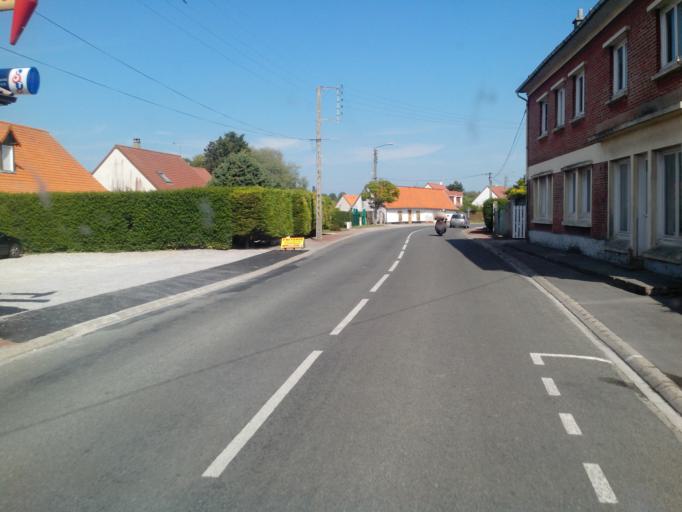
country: FR
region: Nord-Pas-de-Calais
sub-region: Departement du Pas-de-Calais
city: Groffliers
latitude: 50.3835
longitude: 1.6188
